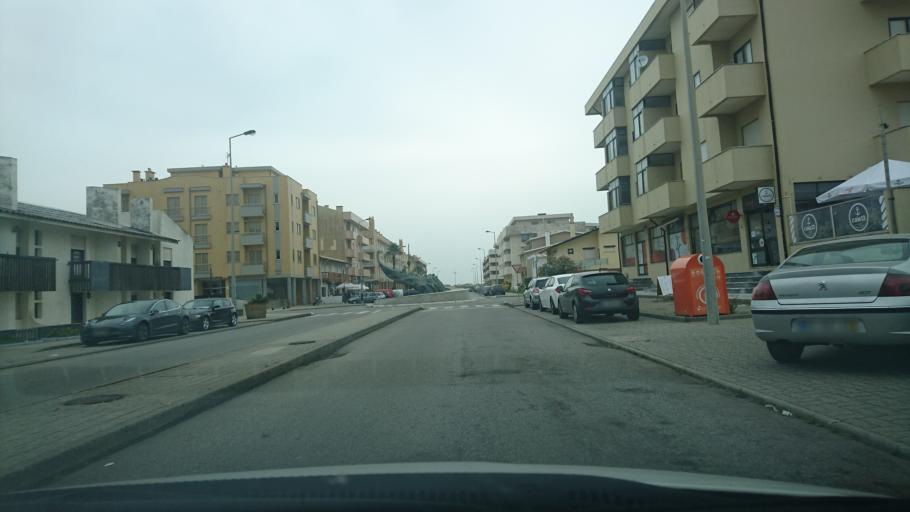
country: PT
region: Aveiro
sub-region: Ovar
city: Esmoriz
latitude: 40.9559
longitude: -8.6532
